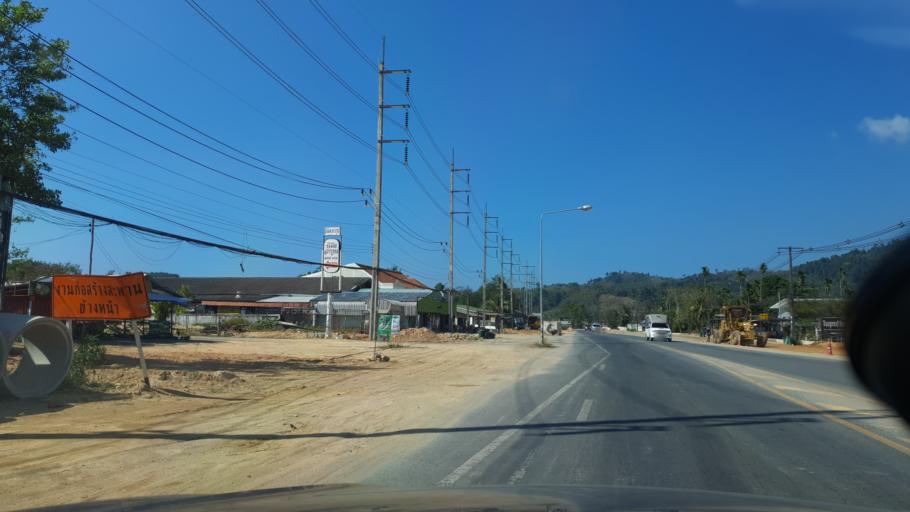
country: TH
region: Phangnga
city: Ban Khao Lak
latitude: 8.5971
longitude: 98.2557
